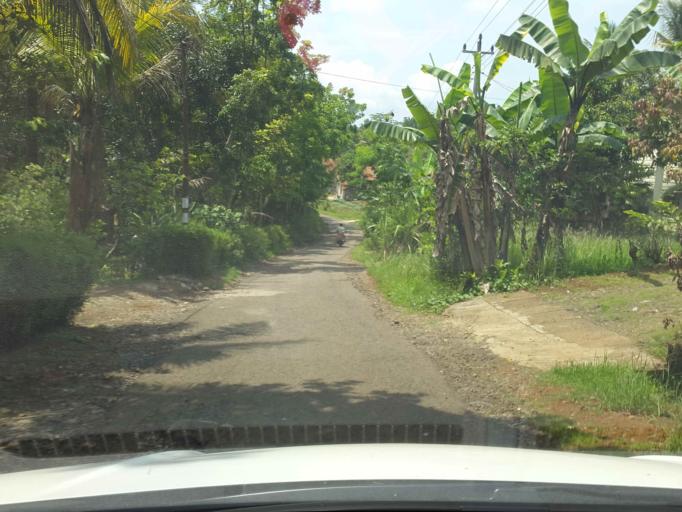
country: ID
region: Central Java
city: Bakung
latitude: -7.3429
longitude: 108.6807
